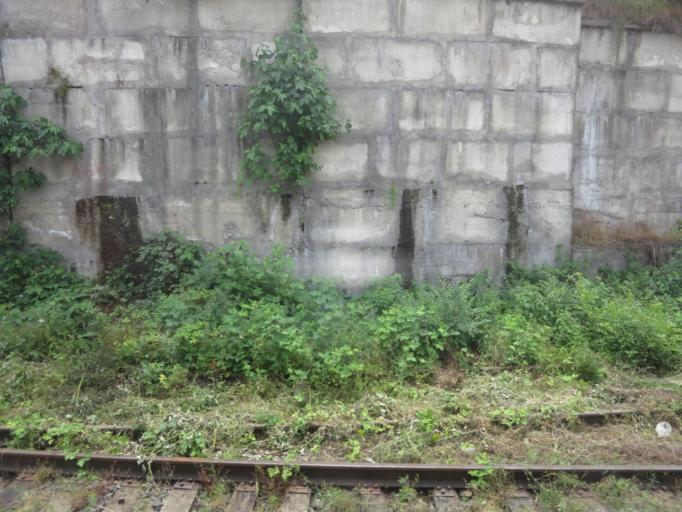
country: GE
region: Mtskheta-Mtianeti
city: Mtskheta
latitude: 41.8375
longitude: 44.7048
